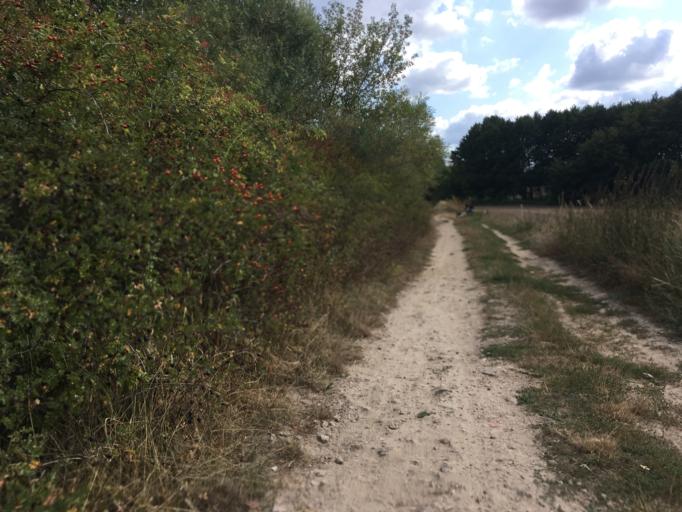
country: DE
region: Berlin
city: Karow
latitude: 52.6019
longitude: 13.4874
